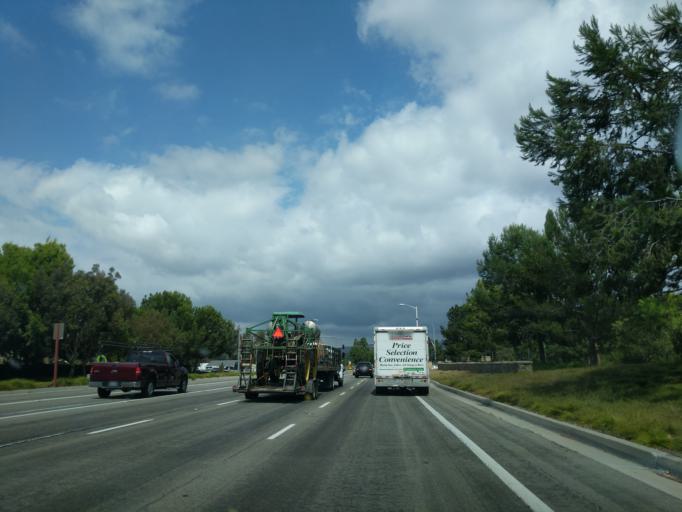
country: US
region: California
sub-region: Orange County
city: Irvine
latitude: 33.7011
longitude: -117.7571
